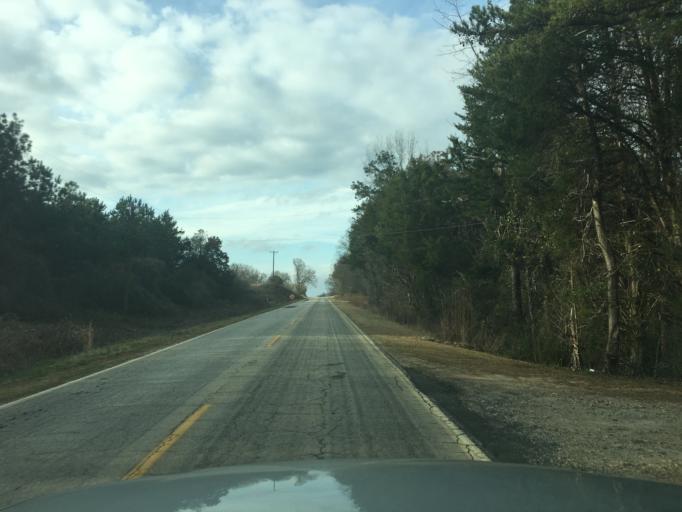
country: US
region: South Carolina
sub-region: Abbeville County
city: Due West
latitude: 34.3427
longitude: -82.4931
